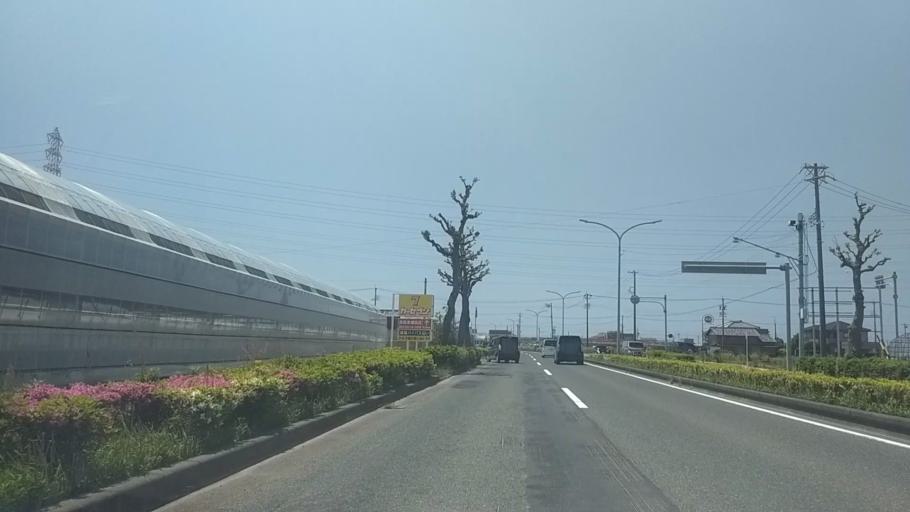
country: JP
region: Shizuoka
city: Hamamatsu
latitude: 34.7357
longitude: 137.6624
